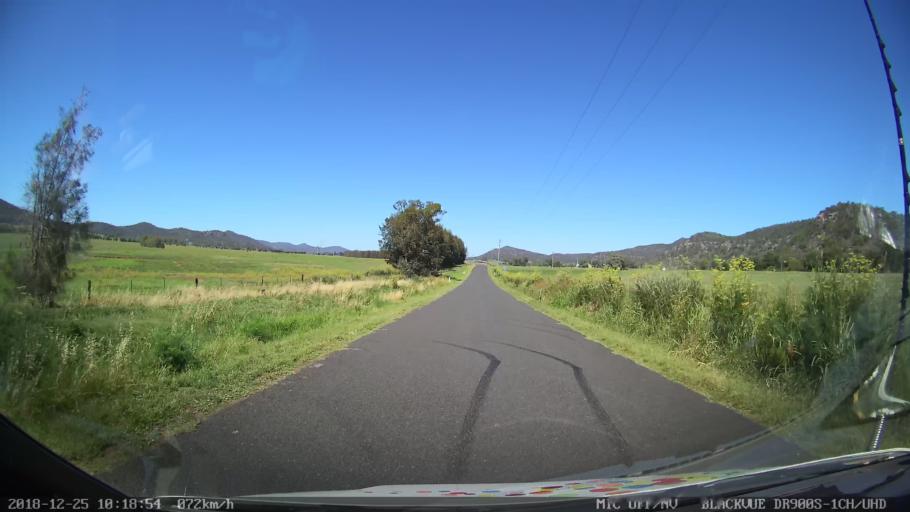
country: AU
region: New South Wales
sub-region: Muswellbrook
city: Denman
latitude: -32.3472
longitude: 150.5642
